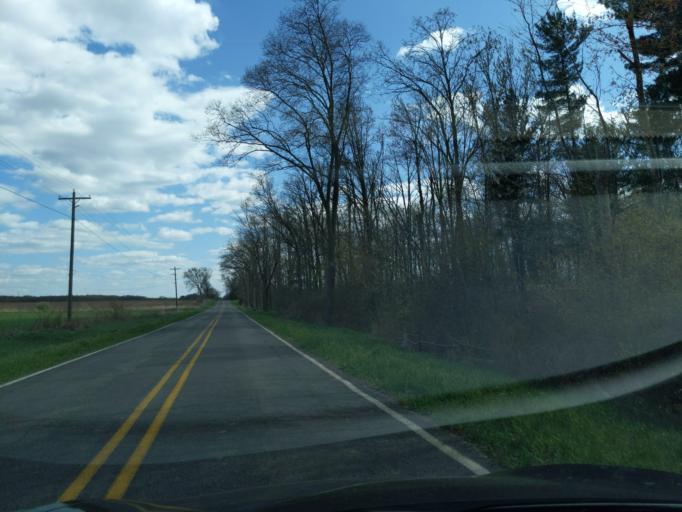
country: US
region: Michigan
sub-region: Ingham County
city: Leslie
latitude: 42.4094
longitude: -84.5416
